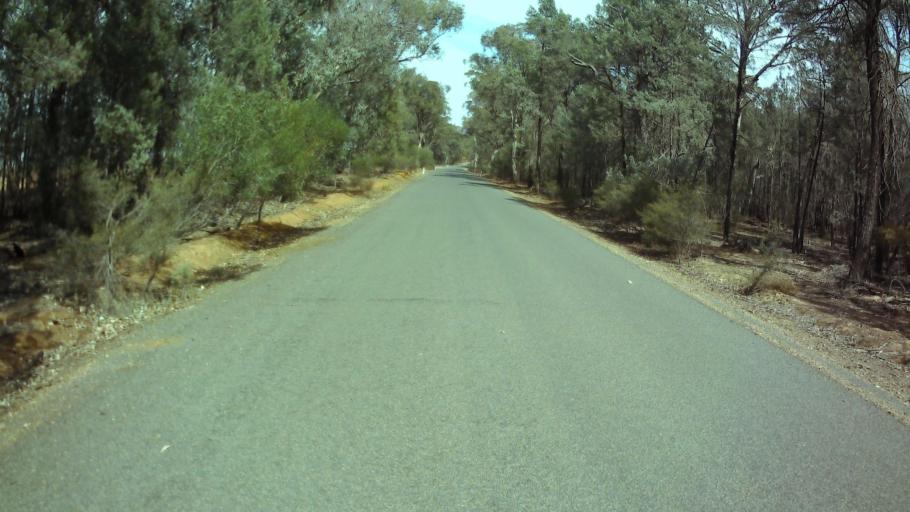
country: AU
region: New South Wales
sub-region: Weddin
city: Grenfell
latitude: -33.8050
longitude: 148.0355
